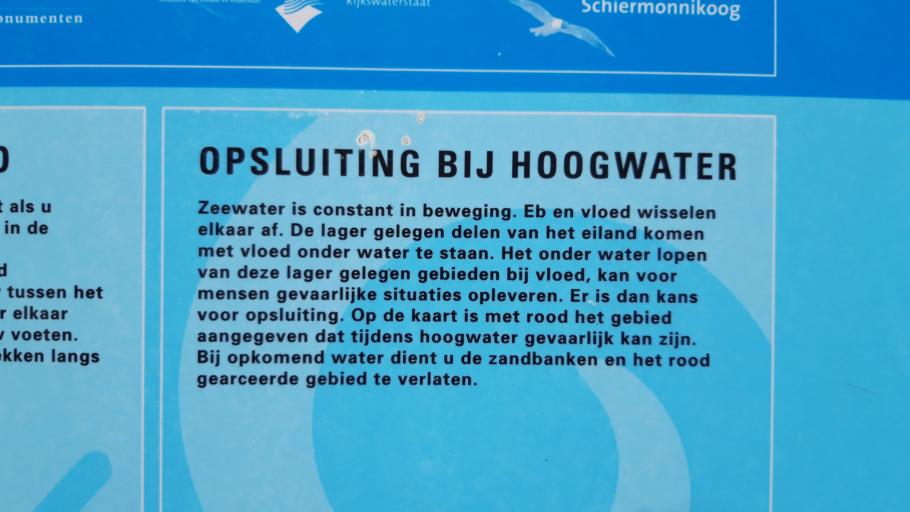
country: NL
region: Friesland
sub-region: Gemeente Schiermonnikoog
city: Schiermonnikoog
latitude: 53.4773
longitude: 6.1383
